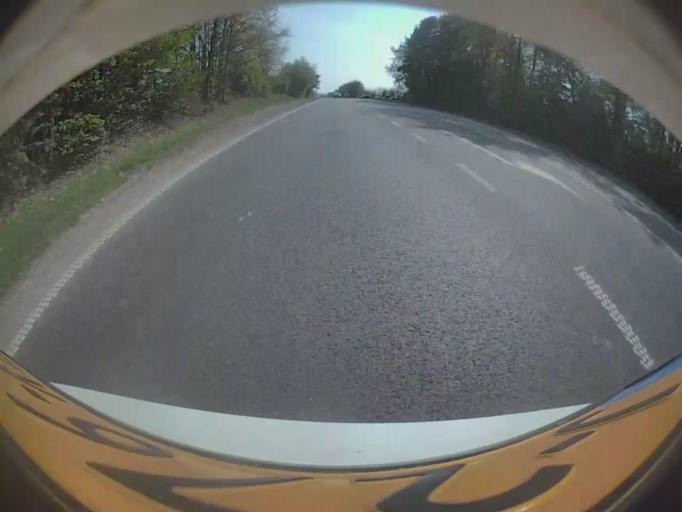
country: BE
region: Wallonia
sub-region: Province de Namur
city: Ciney
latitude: 50.3120
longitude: 5.1245
